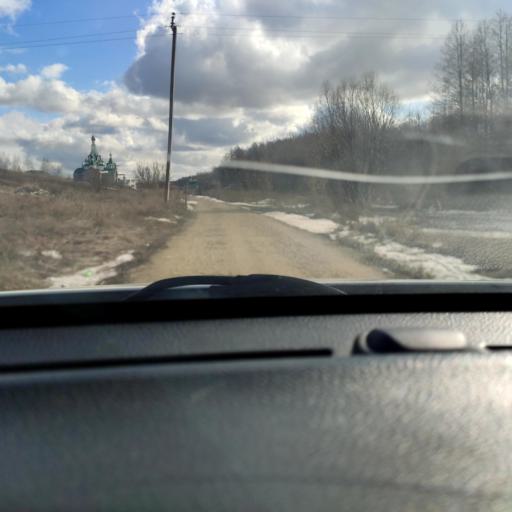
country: RU
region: Voronezj
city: Novaya Usman'
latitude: 51.6839
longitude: 39.3917
